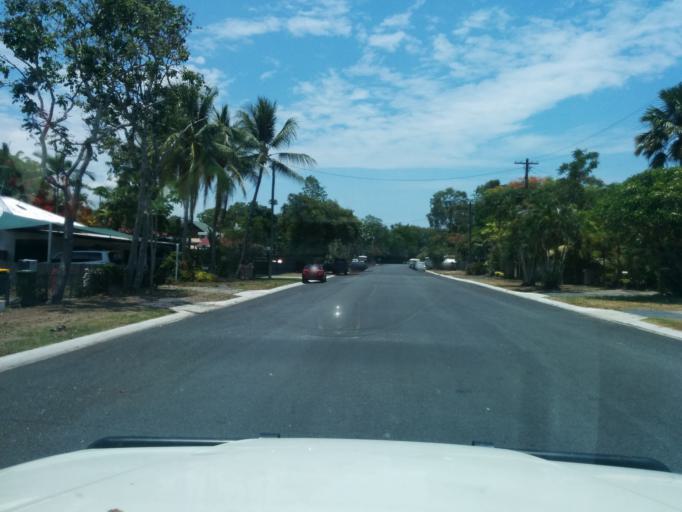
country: AU
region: Queensland
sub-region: Cairns
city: Yorkeys Knob
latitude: -16.8315
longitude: 145.7356
